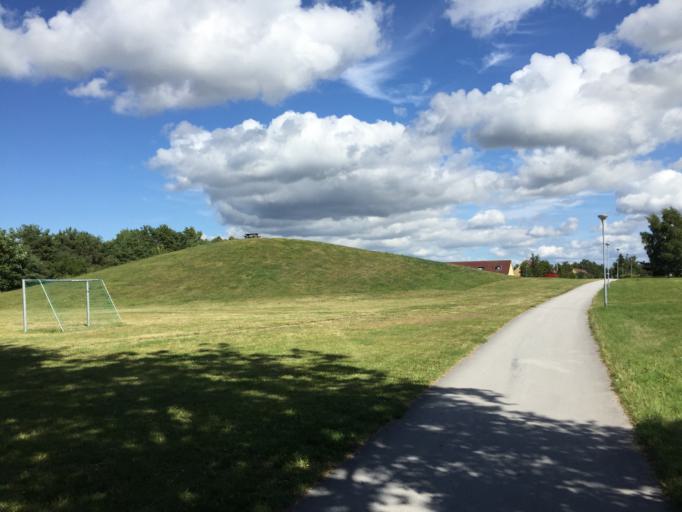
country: SE
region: Gotland
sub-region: Gotland
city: Visby
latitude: 57.6136
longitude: 18.2963
